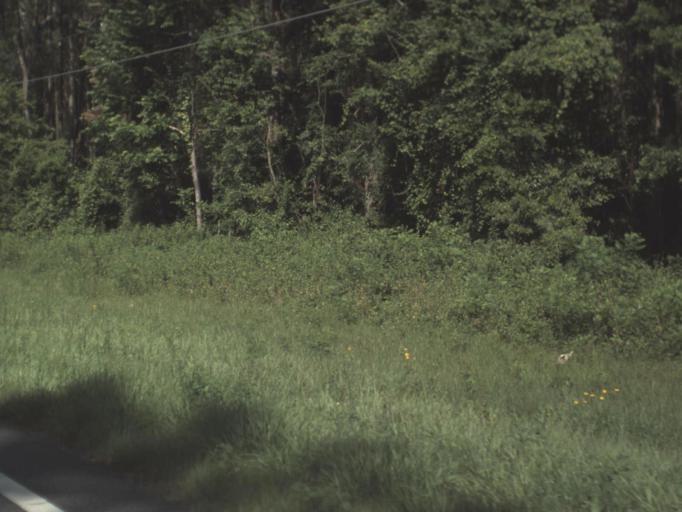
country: US
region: Florida
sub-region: Madison County
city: Madison
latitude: 30.5089
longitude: -83.3761
